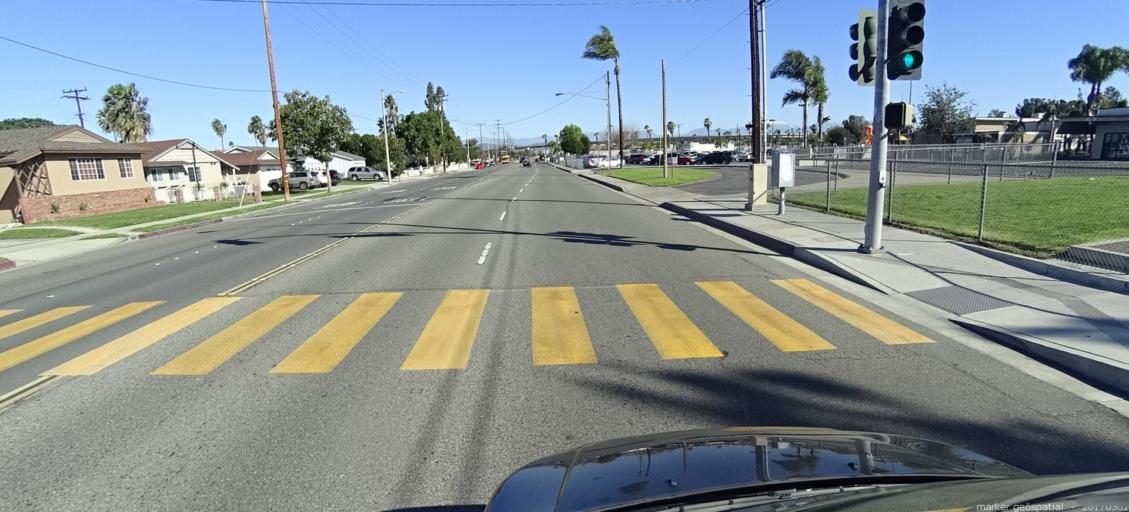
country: US
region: California
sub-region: Orange County
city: Placentia
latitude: 33.8447
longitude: -117.8804
